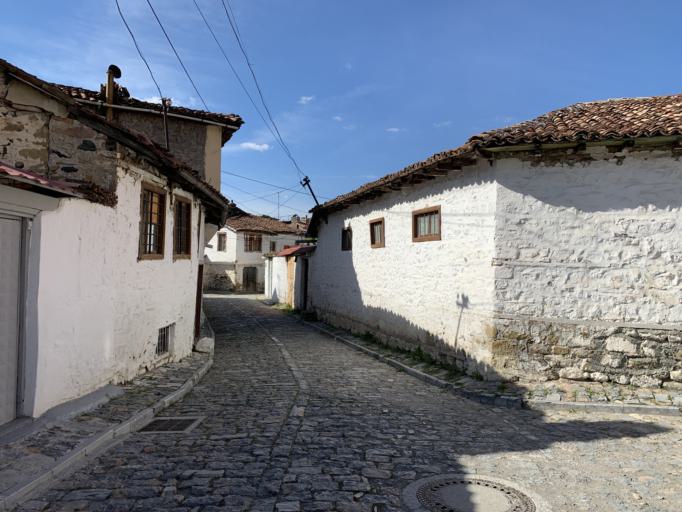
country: AL
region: Korce
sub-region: Rrethi i Korces
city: Korce
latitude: 40.6142
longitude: 20.7831
